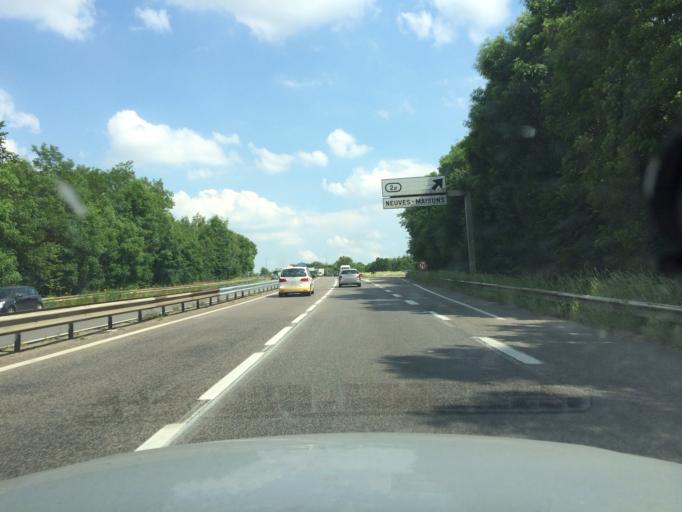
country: FR
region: Lorraine
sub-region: Departement de Meurthe-et-Moselle
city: Chavigny
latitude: 48.6482
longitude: 6.1360
